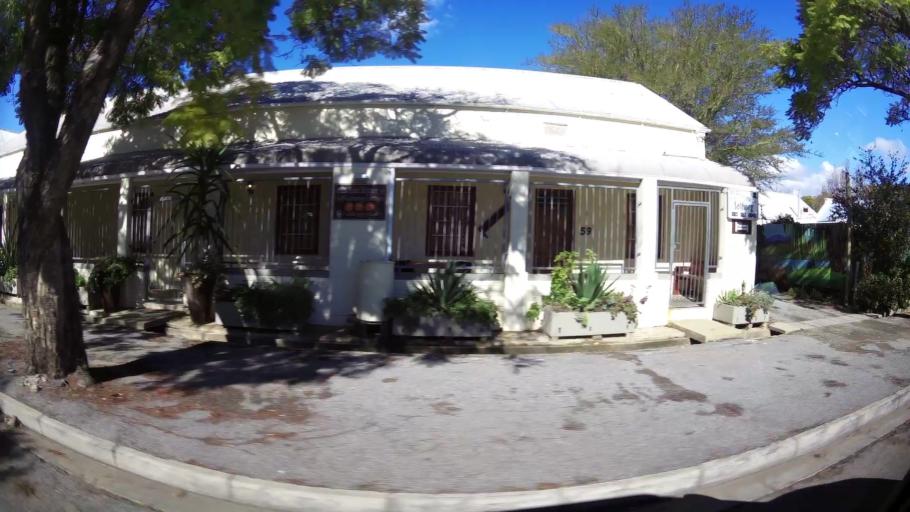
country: ZA
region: Western Cape
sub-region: Cape Winelands District Municipality
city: Ashton
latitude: -33.8013
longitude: 19.8846
